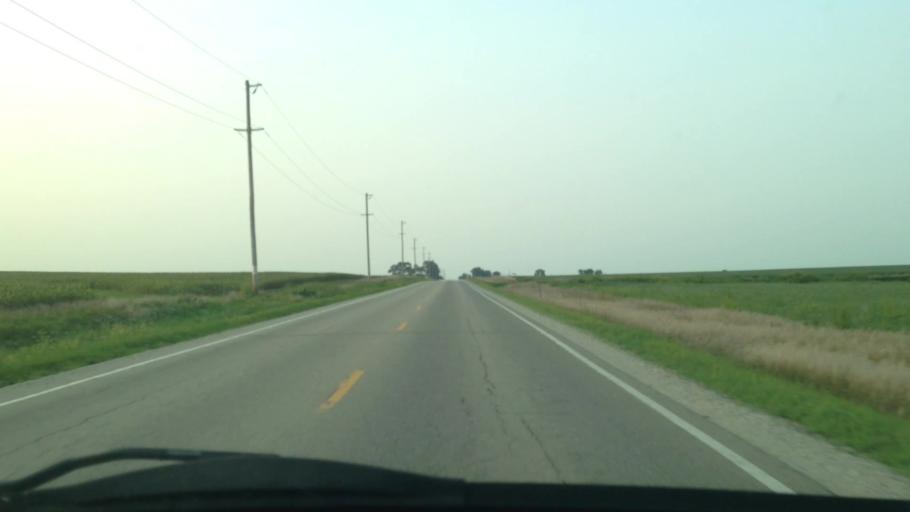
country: US
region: Iowa
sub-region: Iowa County
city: Marengo
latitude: 41.9554
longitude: -92.0852
